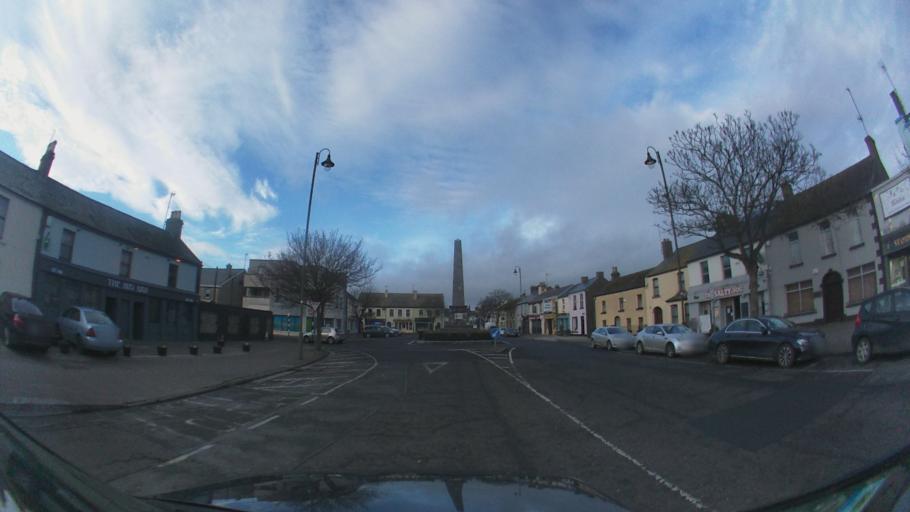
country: IE
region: Leinster
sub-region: Fingal County
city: Skerries
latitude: 53.5804
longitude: -6.1068
